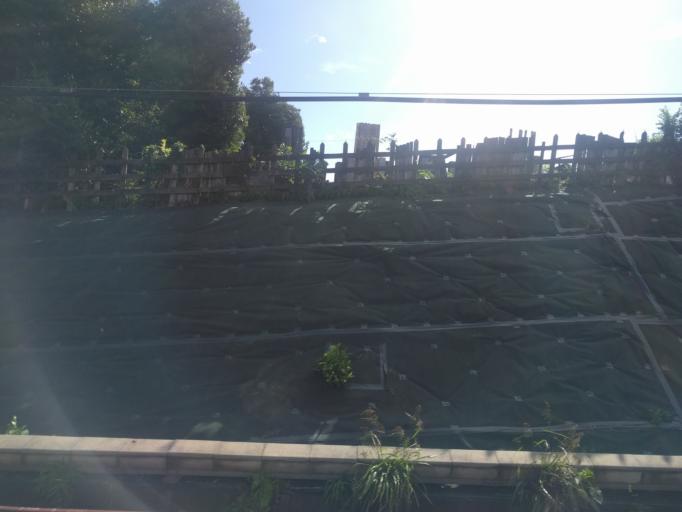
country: JP
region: Tokyo
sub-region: Machida-shi
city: Machida
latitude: 35.5389
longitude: 139.4426
